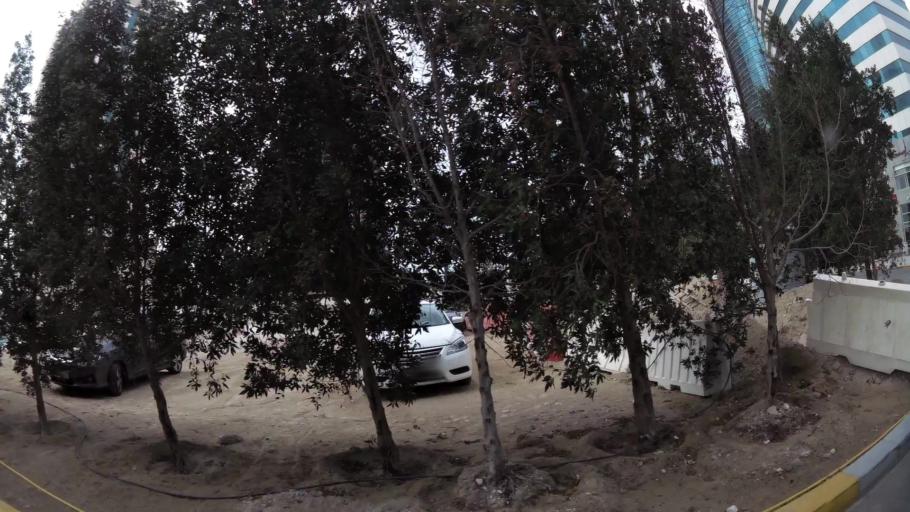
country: AE
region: Abu Dhabi
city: Abu Dhabi
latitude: 24.4313
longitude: 54.4345
